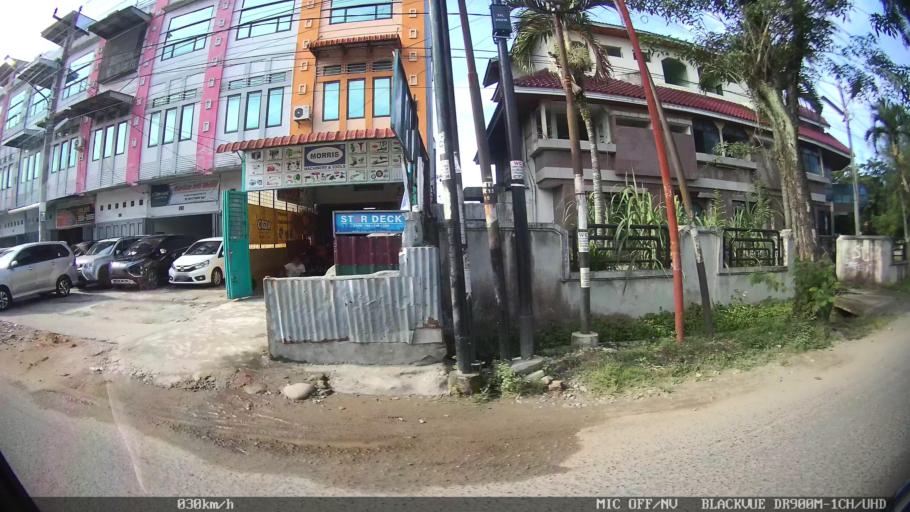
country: ID
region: North Sumatra
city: Medan
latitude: 3.6036
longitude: 98.6558
